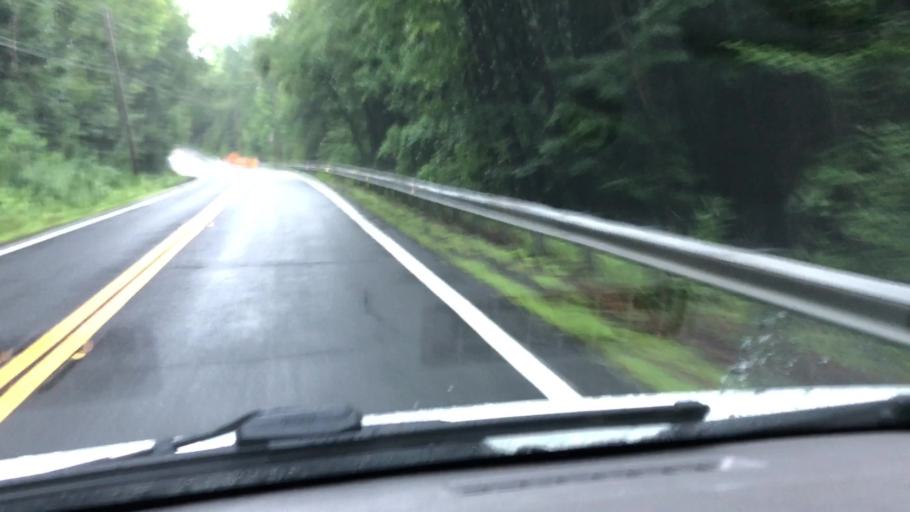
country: US
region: Massachusetts
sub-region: Hampshire County
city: Chesterfield
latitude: 42.3468
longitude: -72.8965
